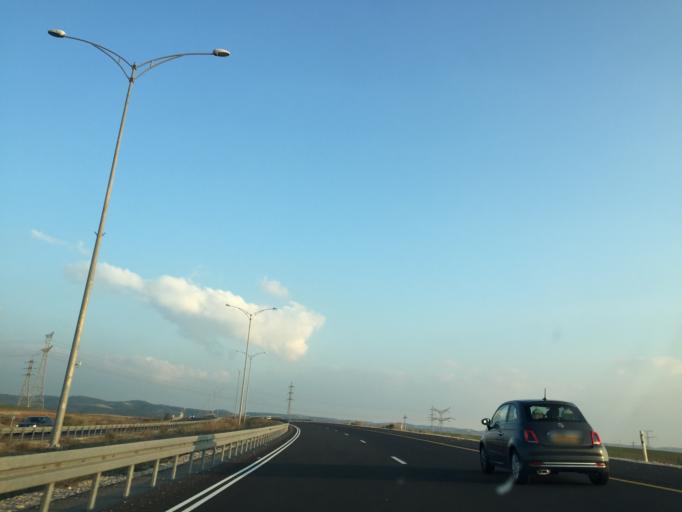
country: IL
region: Southern District
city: Lehavim
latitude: 31.3923
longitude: 34.7924
